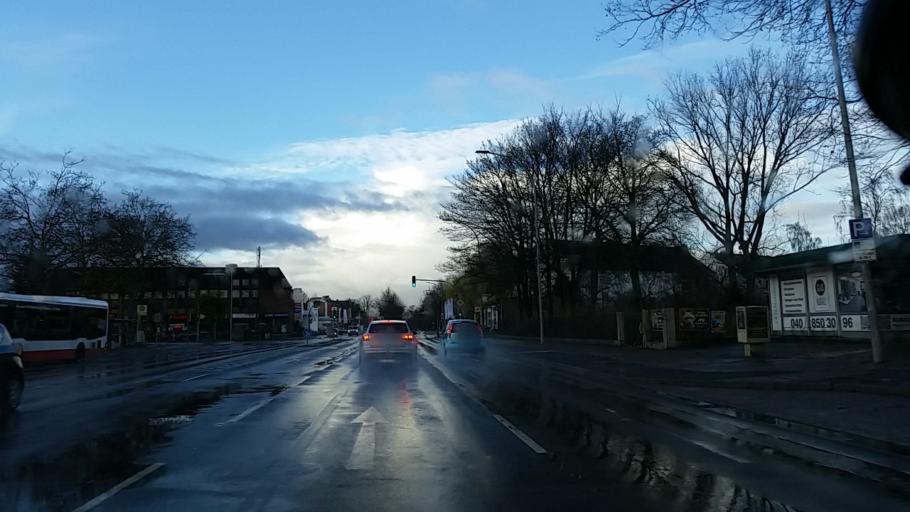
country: DE
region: Schleswig-Holstein
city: Halstenbek
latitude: 53.5987
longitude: 9.8507
